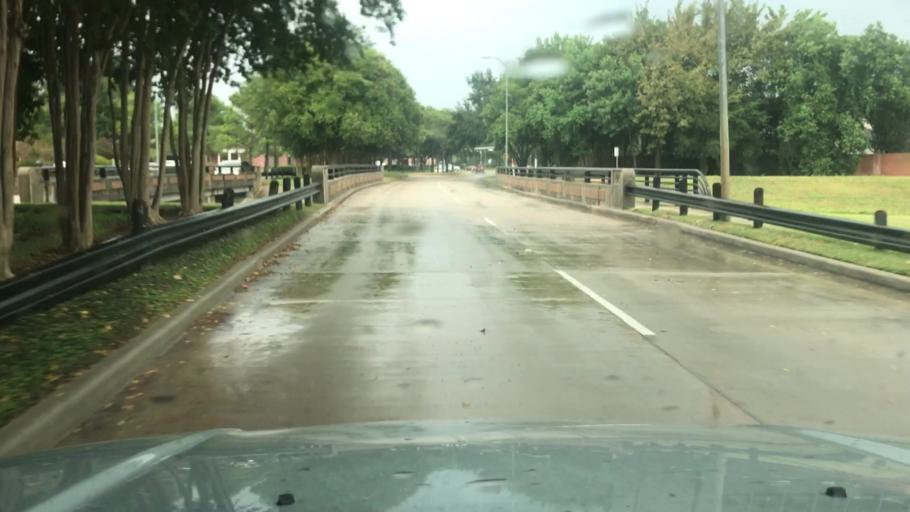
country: US
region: Texas
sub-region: Fort Bend County
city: Cinco Ranch
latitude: 29.7393
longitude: -95.7842
